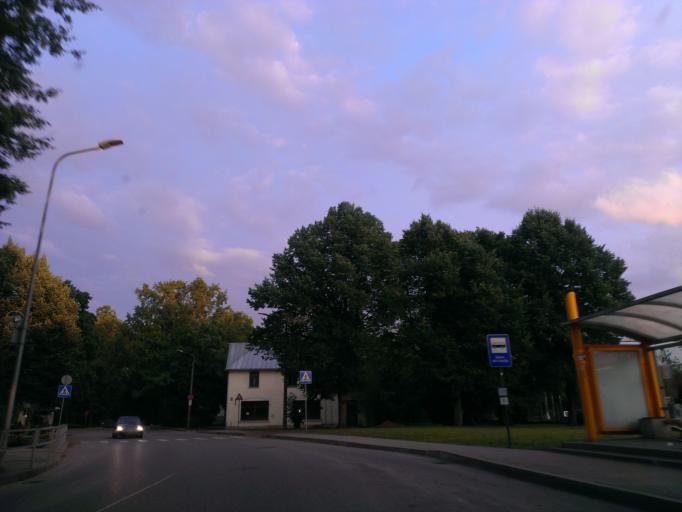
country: LV
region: Ogre
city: Ogre
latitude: 56.8160
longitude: 24.6029
